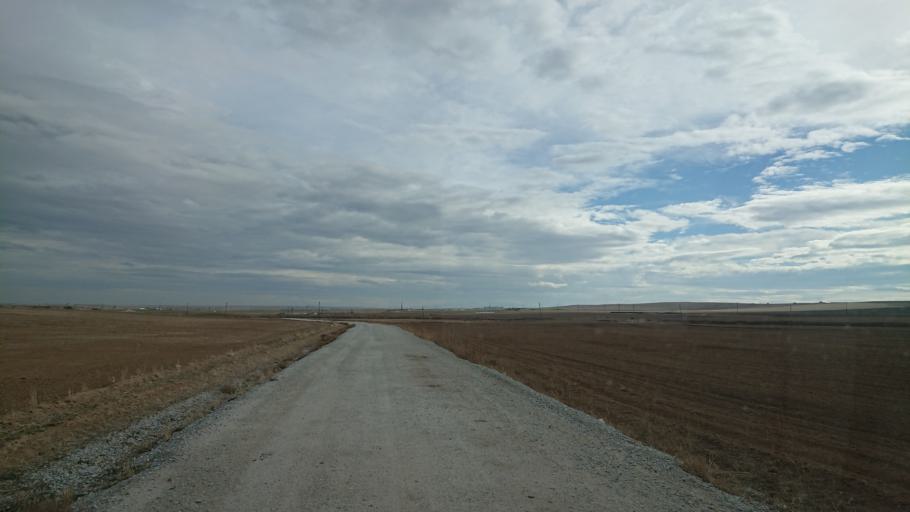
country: TR
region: Aksaray
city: Sultanhani
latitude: 38.1356
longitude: 33.5550
